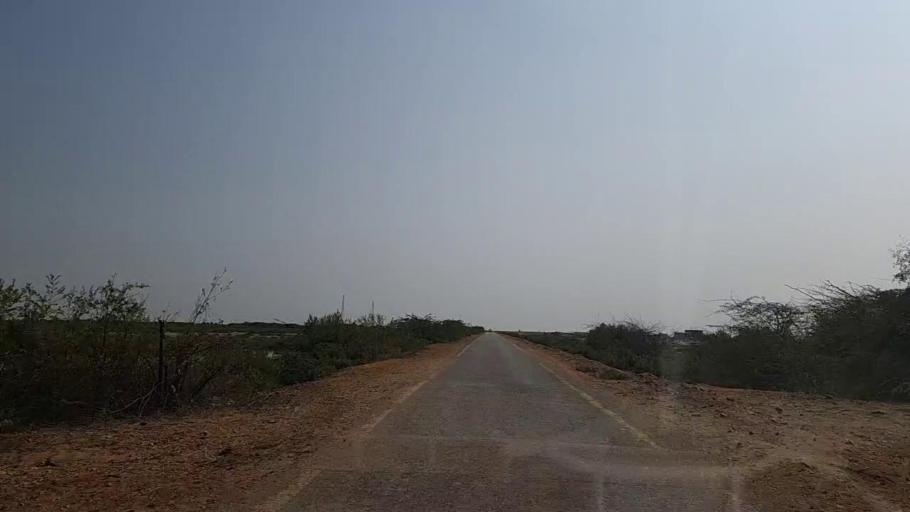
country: PK
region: Sindh
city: Chuhar Jamali
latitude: 24.1732
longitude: 67.8921
